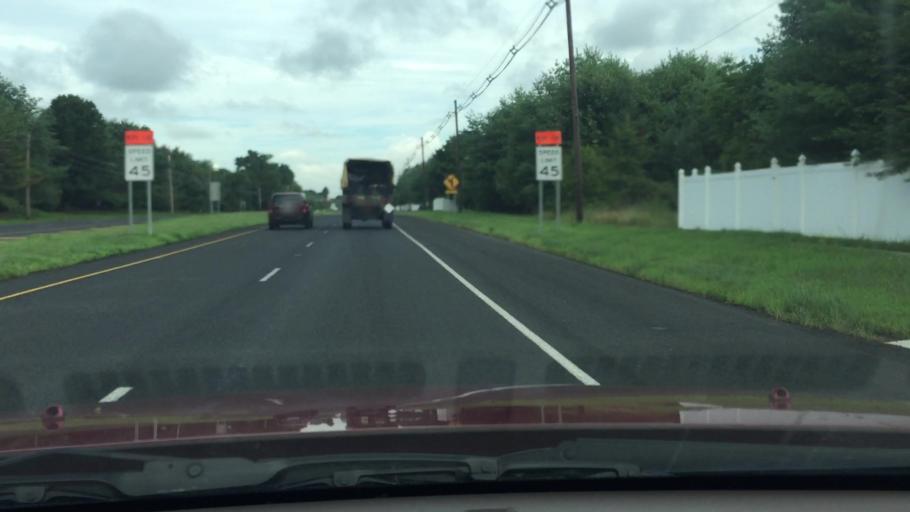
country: US
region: New Jersey
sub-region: Burlington County
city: Fort Dix
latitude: 40.0814
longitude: -74.6675
